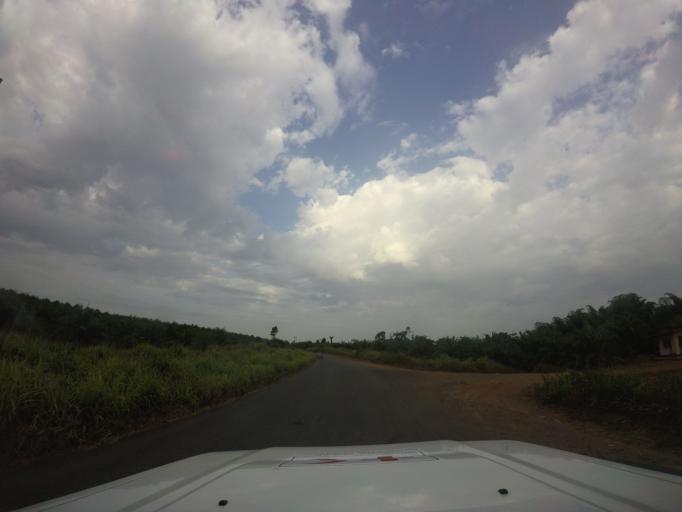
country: LR
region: Bomi
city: Tubmanburg
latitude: 6.7132
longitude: -10.9395
